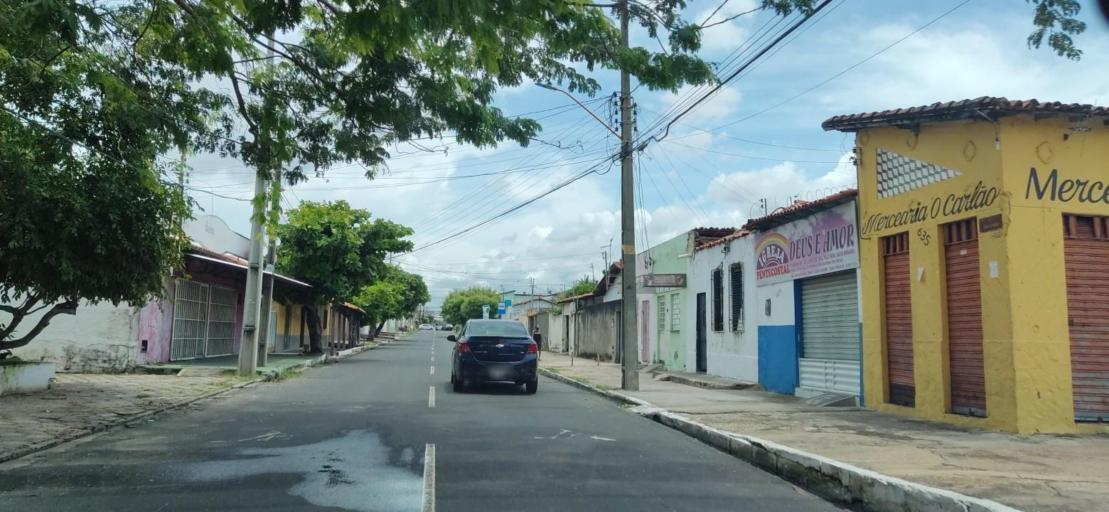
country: BR
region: Piaui
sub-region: Teresina
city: Teresina
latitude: -5.0759
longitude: -42.8054
